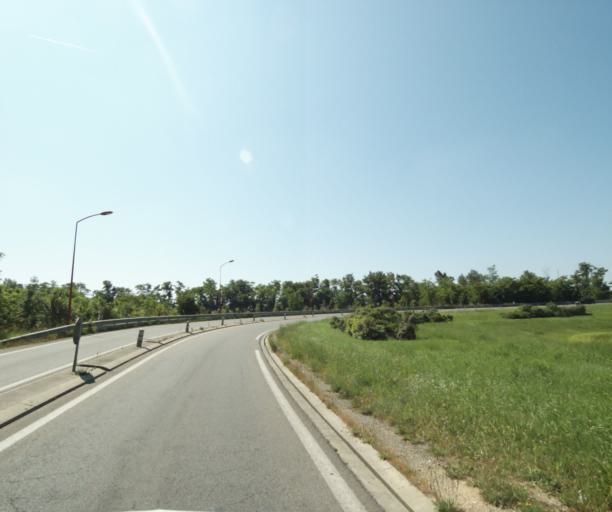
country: FR
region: Midi-Pyrenees
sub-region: Departement du Tarn-et-Garonne
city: Montauban
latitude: 44.0187
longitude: 1.3277
